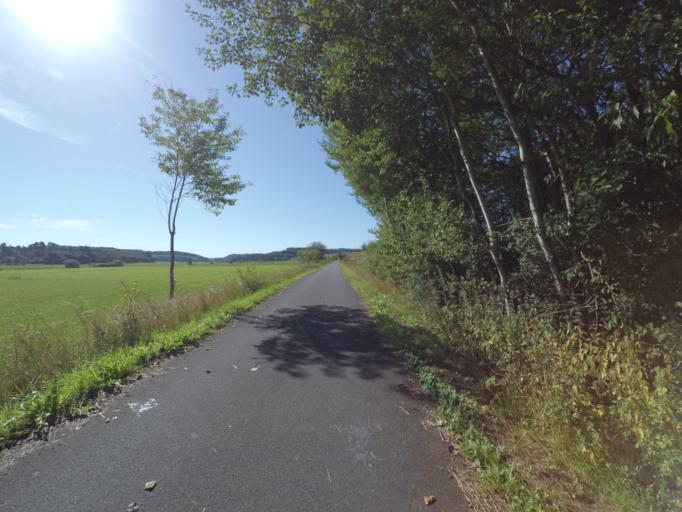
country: DE
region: Rheinland-Pfalz
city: Udler
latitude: 50.1460
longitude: 6.8788
